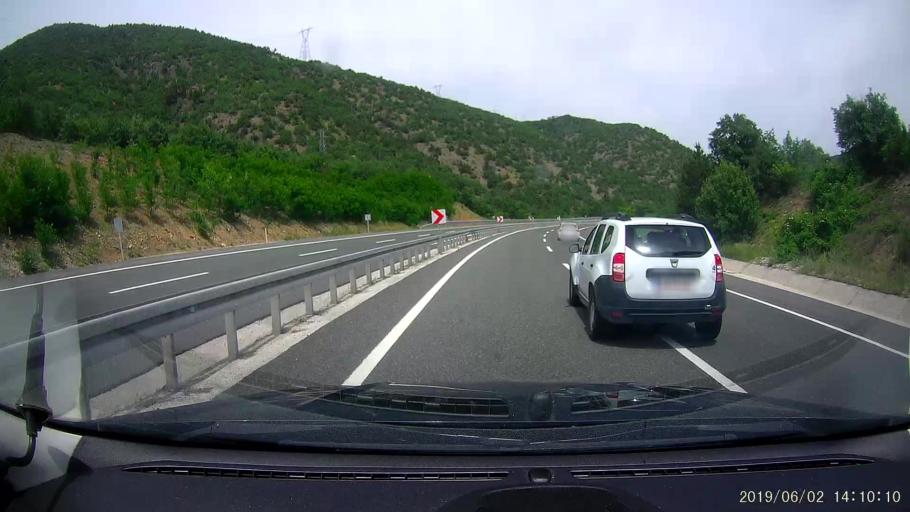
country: TR
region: Cankiri
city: Ilgaz
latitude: 40.9024
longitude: 33.7541
